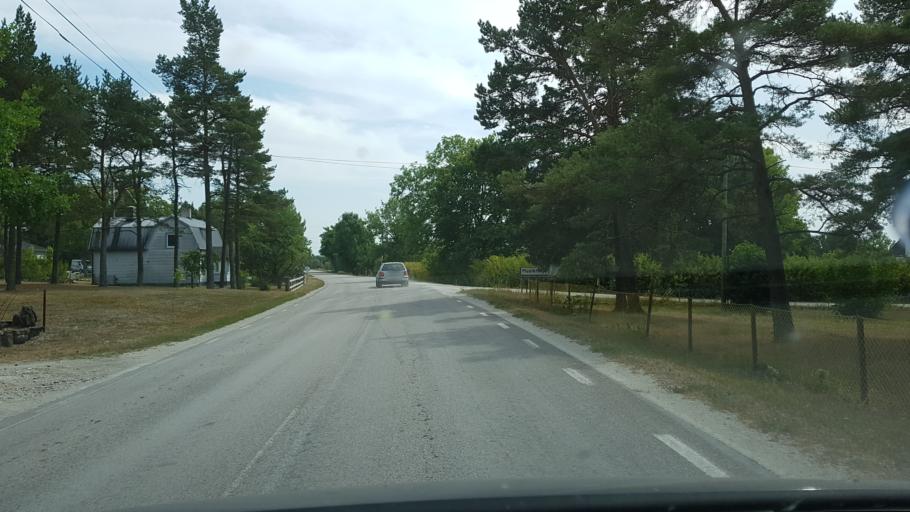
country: SE
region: Gotland
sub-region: Gotland
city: Slite
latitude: 57.7360
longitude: 18.7377
